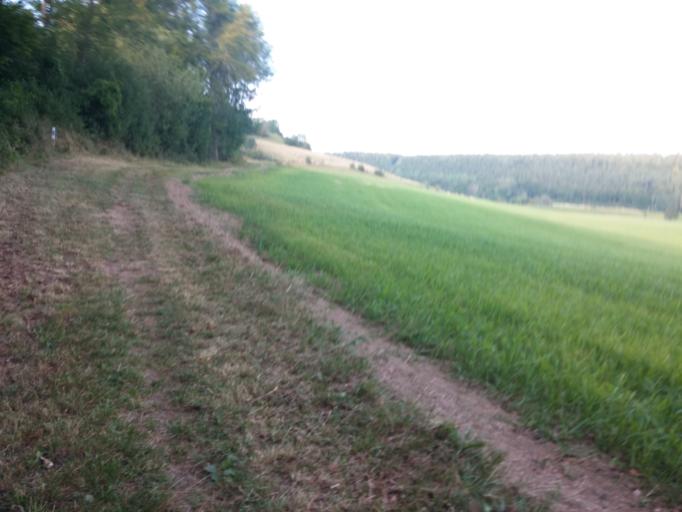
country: DE
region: Bavaria
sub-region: Swabia
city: Woringen
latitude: 47.8668
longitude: 10.1942
